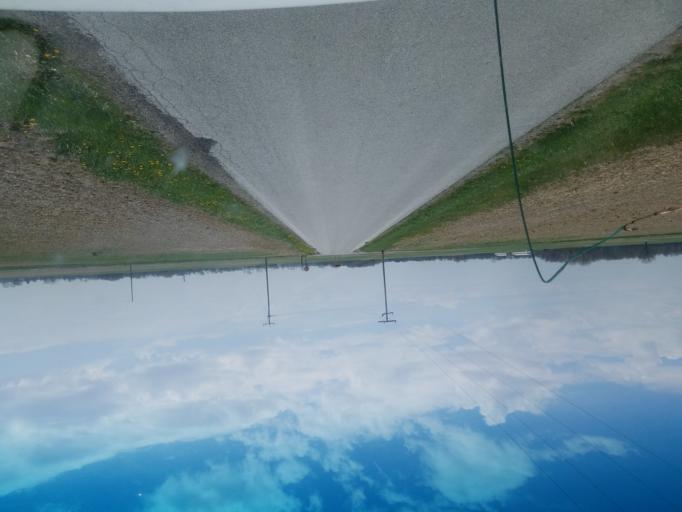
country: US
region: Ohio
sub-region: Hardin County
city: Kenton
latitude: 40.6734
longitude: -83.5630
